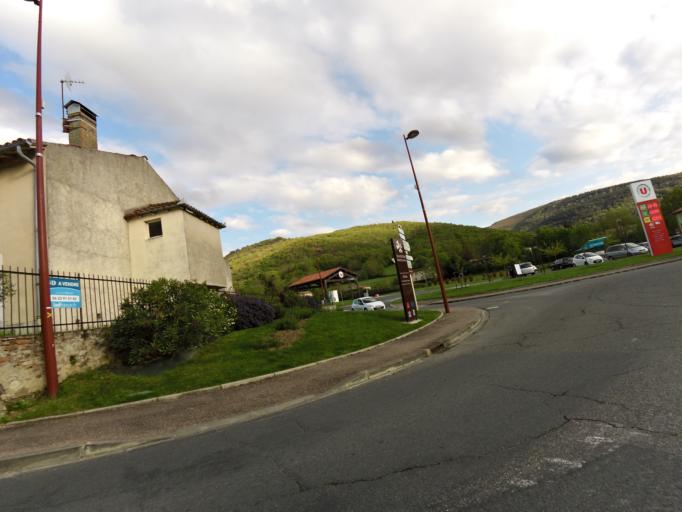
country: FR
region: Midi-Pyrenees
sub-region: Departement du Tarn
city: Soreze
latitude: 43.4508
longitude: 2.0638
